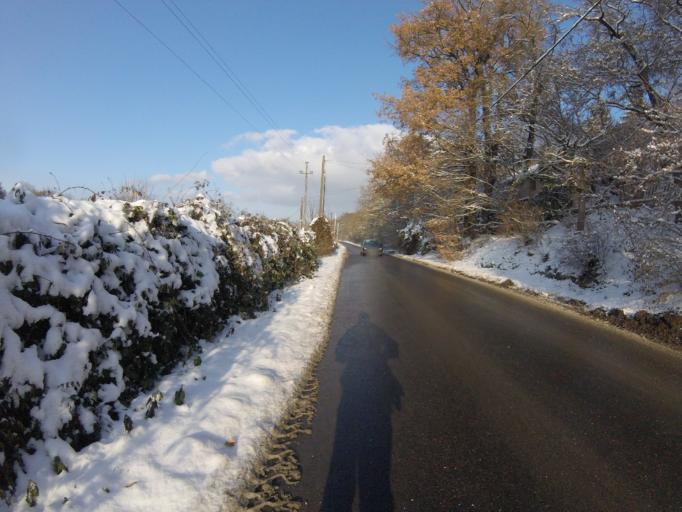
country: HU
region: Pest
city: Budakeszi
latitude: 47.4965
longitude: 18.9225
